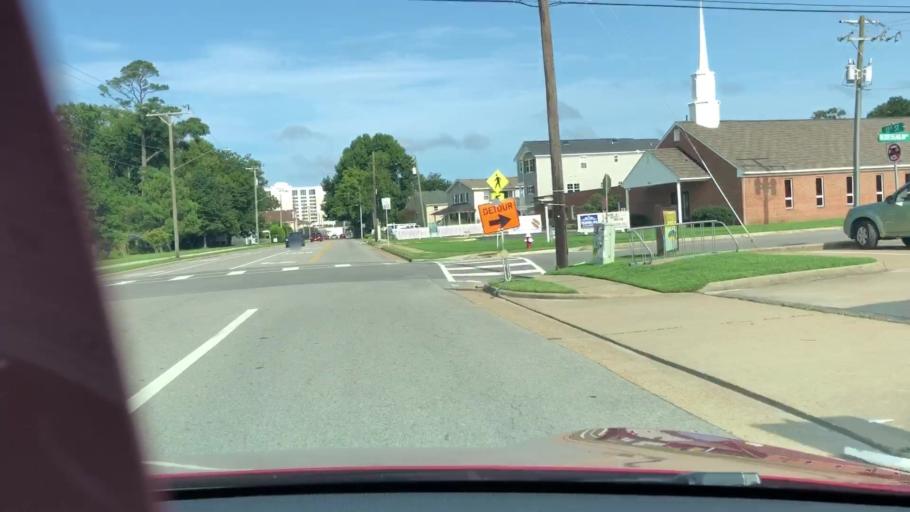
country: US
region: Virginia
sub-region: City of Virginia Beach
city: Virginia Beach
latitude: 36.8376
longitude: -75.9797
